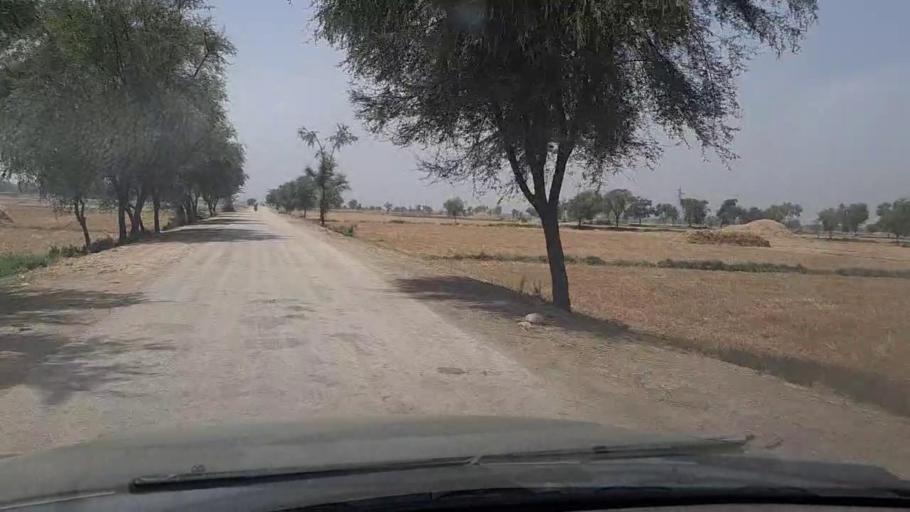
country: PK
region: Sindh
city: Ratodero
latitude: 27.7947
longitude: 68.2446
